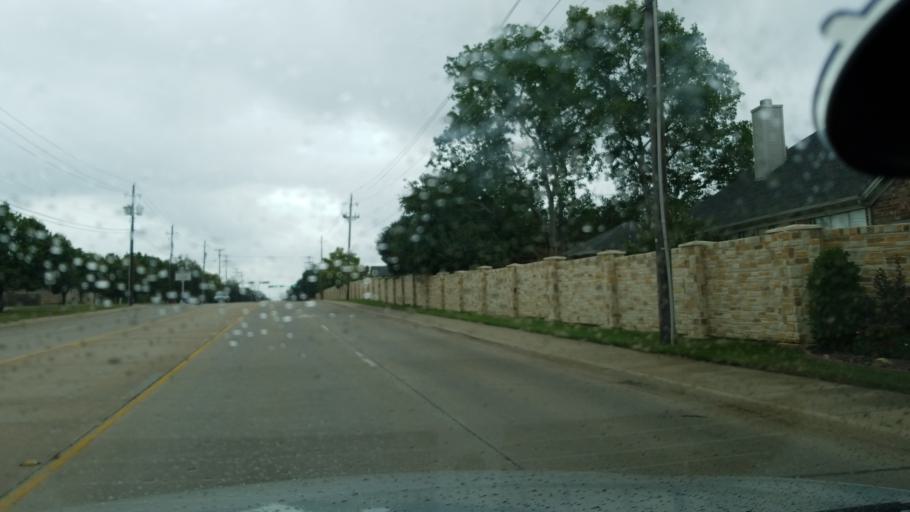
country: US
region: Texas
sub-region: Tarrant County
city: Bedford
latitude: 32.8447
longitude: -97.1268
